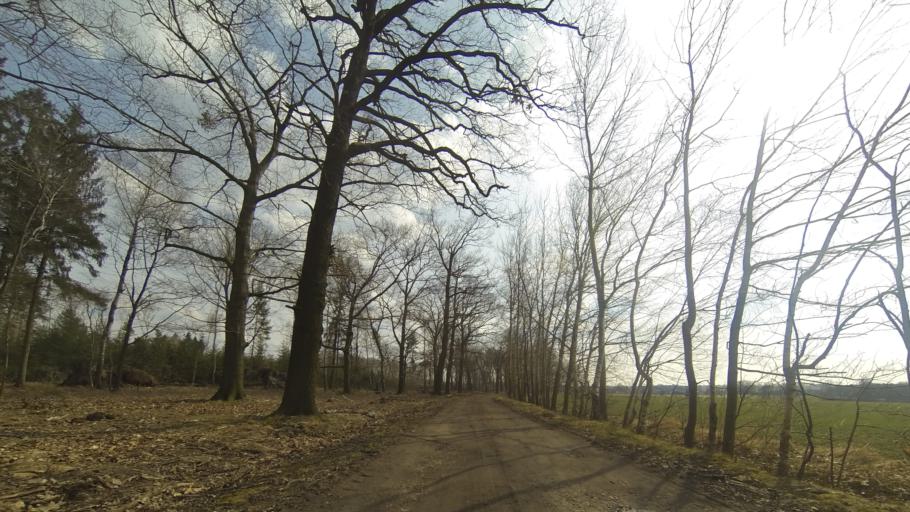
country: DE
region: Saxony
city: Radeburg
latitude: 51.2492
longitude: 13.7037
